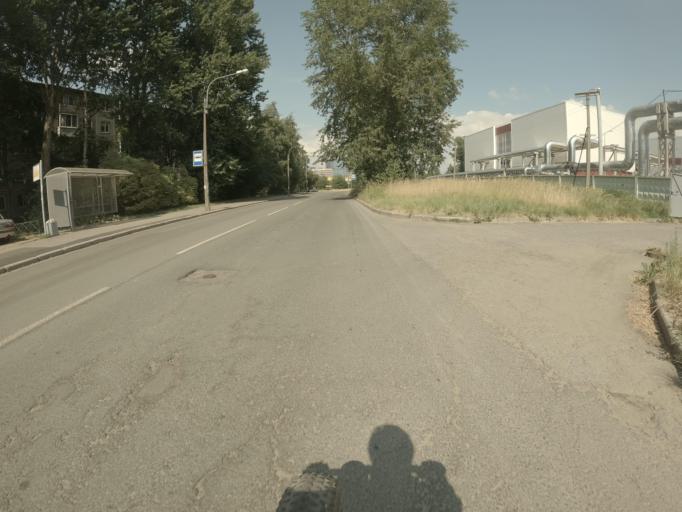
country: RU
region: St.-Petersburg
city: Krasnogvargeisky
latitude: 59.9272
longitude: 30.4318
